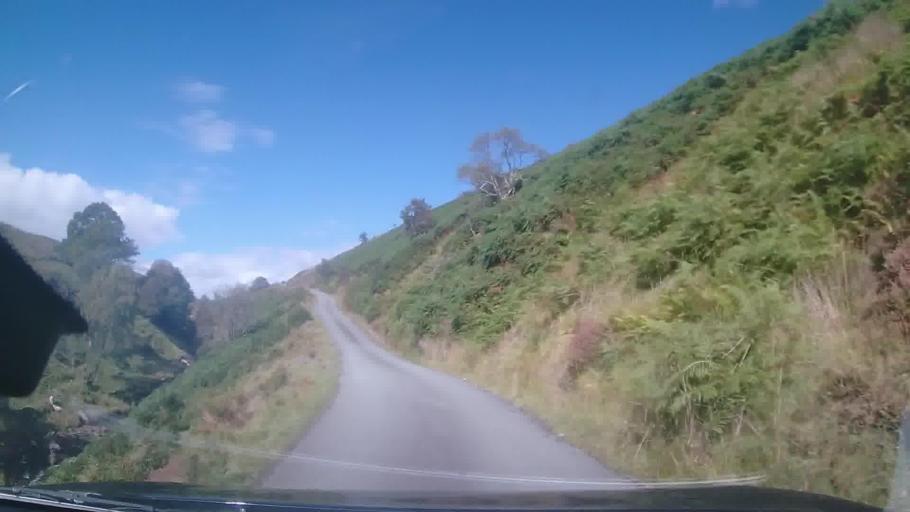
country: GB
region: Wales
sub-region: Gwynedd
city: Bala
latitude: 52.7941
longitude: -3.5647
